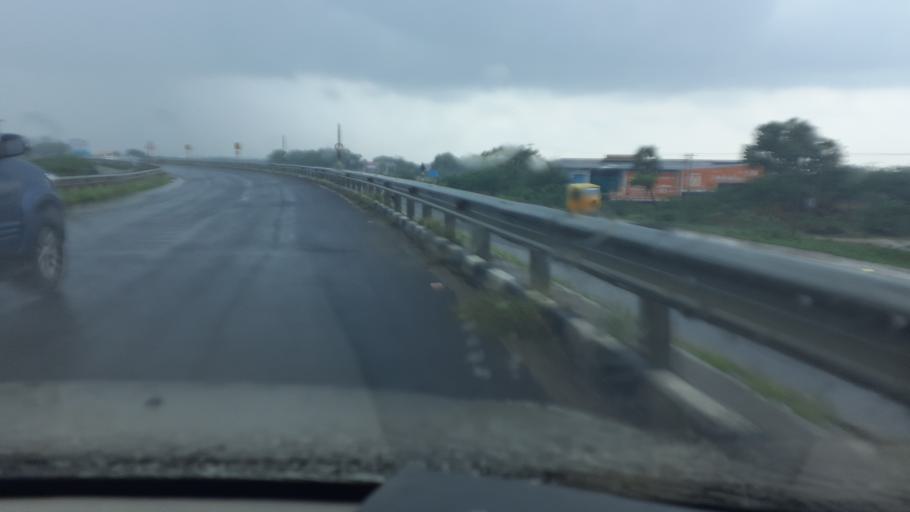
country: IN
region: Tamil Nadu
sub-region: Virudhunagar
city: Virudunagar
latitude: 9.5948
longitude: 77.9445
